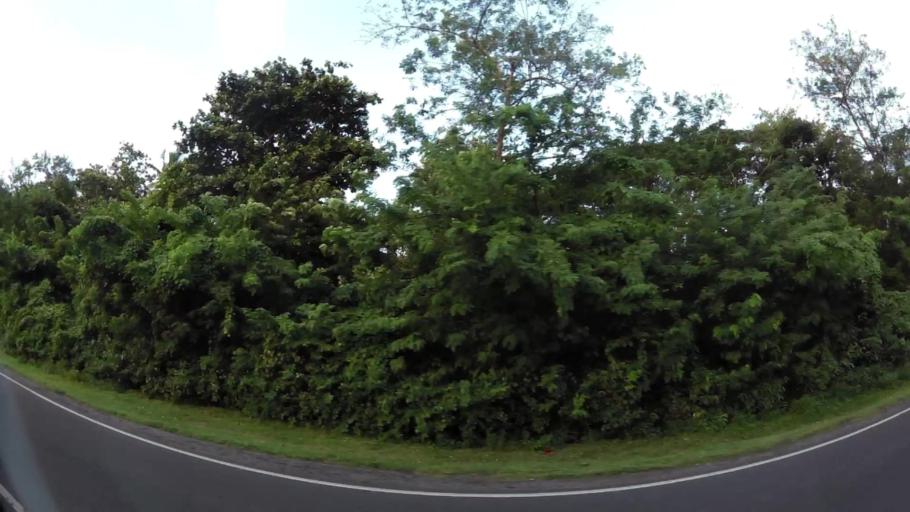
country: LC
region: Castries Quarter
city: Bisee
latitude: 14.0376
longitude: -60.9688
